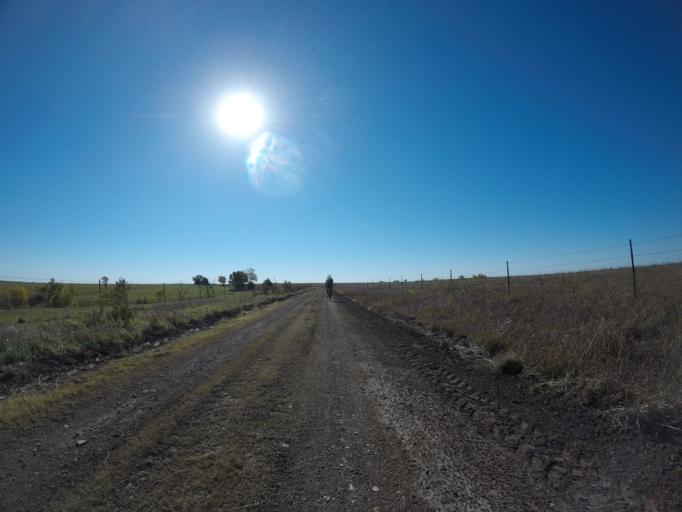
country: US
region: Kansas
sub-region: Wabaunsee County
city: Alma
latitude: 38.8831
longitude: -96.3693
